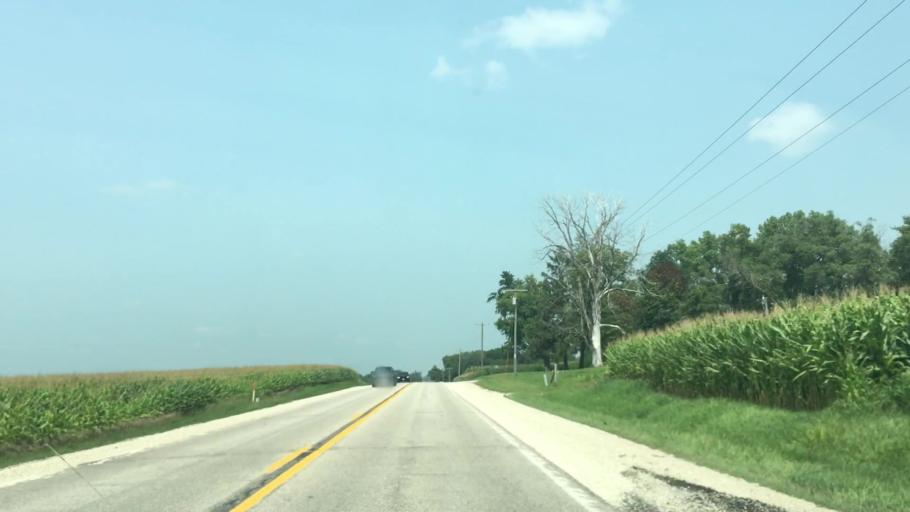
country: US
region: Iowa
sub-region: Benton County
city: Urbana
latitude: 42.3453
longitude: -91.8893
